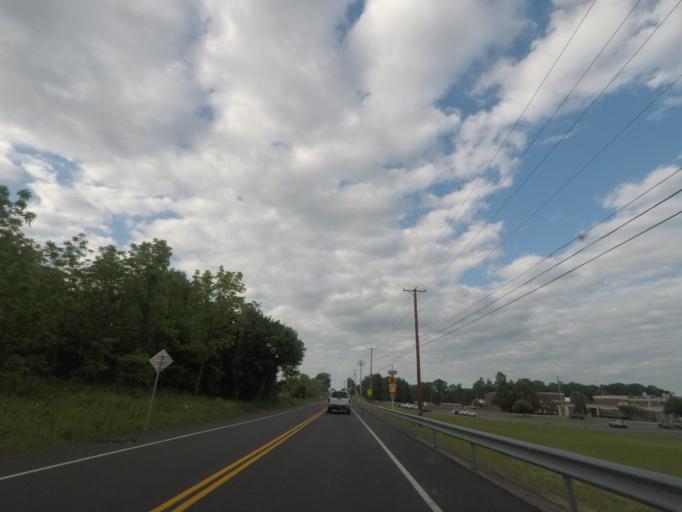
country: US
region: New York
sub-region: Ulster County
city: New Paltz
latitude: 41.7239
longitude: -74.0783
